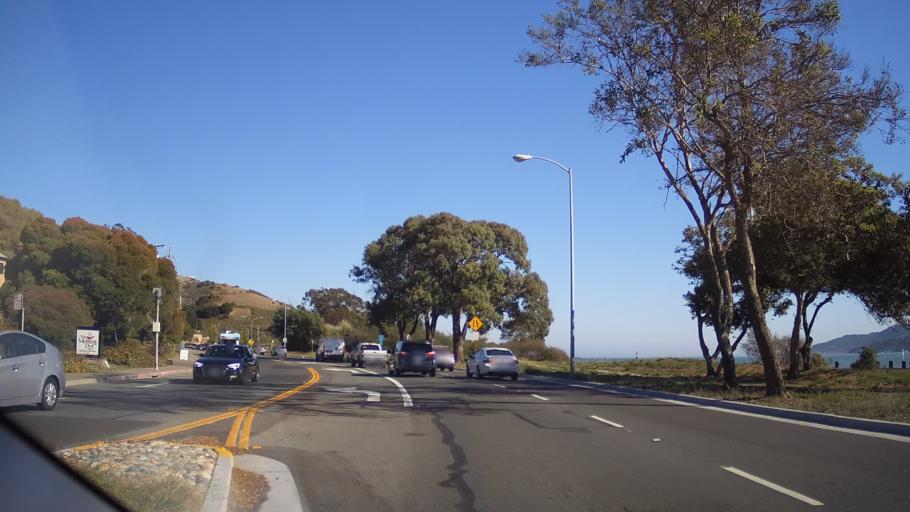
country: US
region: California
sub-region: Marin County
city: Corte Madera
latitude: 37.9445
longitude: -122.5064
